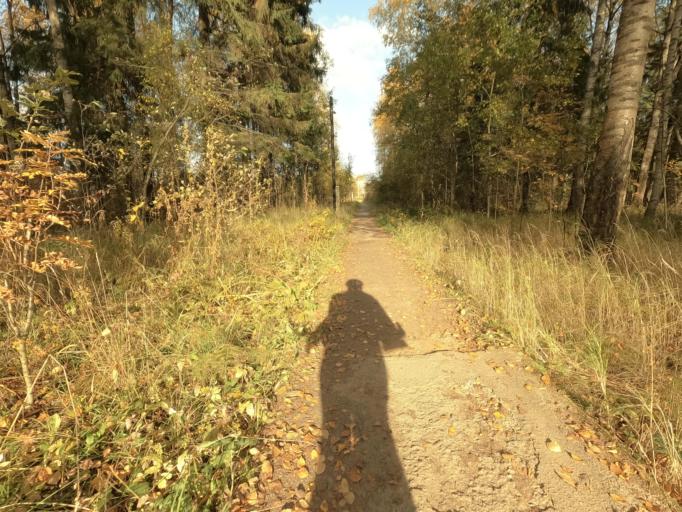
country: RU
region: Leningrad
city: Mga
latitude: 59.7619
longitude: 31.1162
